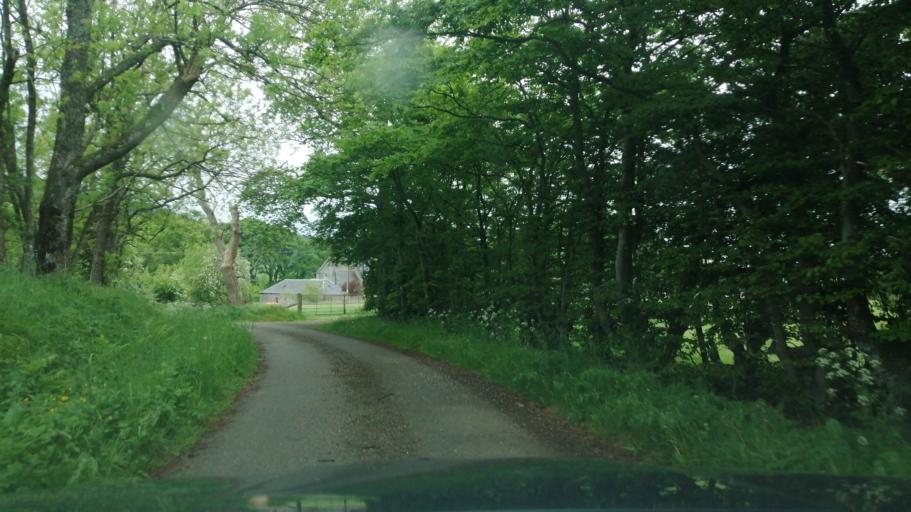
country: GB
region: Scotland
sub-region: Moray
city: Keith
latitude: 57.5535
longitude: -2.8713
